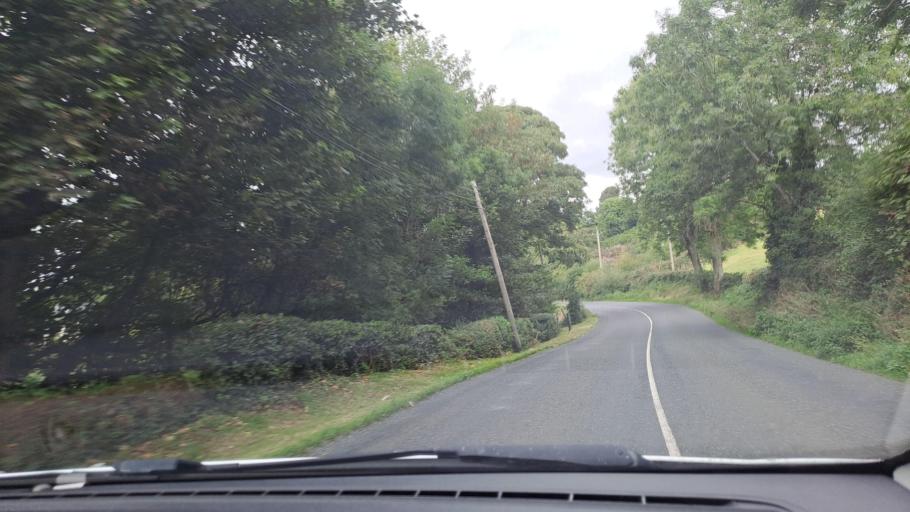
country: IE
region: Ulster
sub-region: An Cabhan
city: Bailieborough
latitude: 54.0033
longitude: -6.9105
